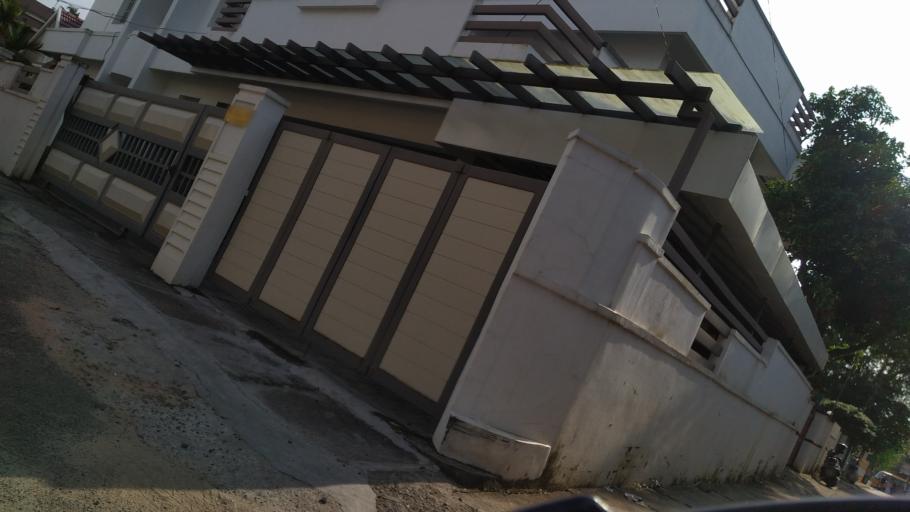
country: IN
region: Kerala
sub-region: Ernakulam
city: Elur
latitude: 10.0021
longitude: 76.2843
